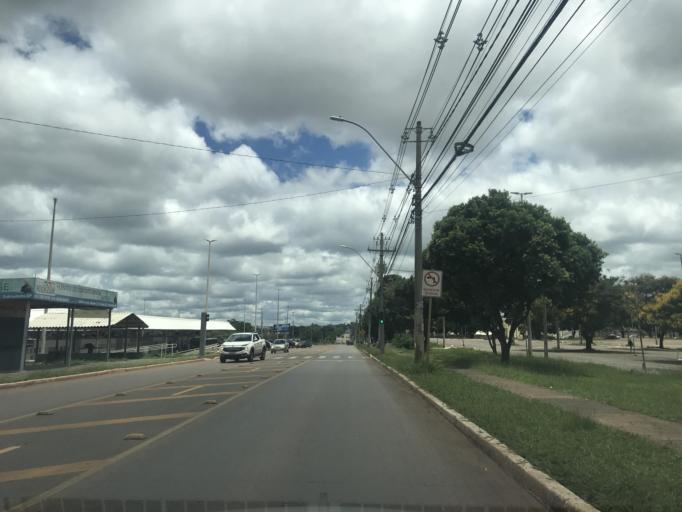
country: BR
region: Federal District
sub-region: Brasilia
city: Brasilia
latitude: -15.6510
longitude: -47.7867
